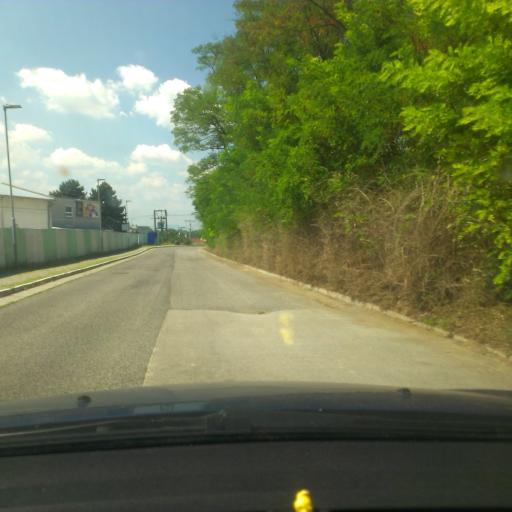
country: SK
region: Trnavsky
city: Hlohovec
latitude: 48.4436
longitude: 17.8125
